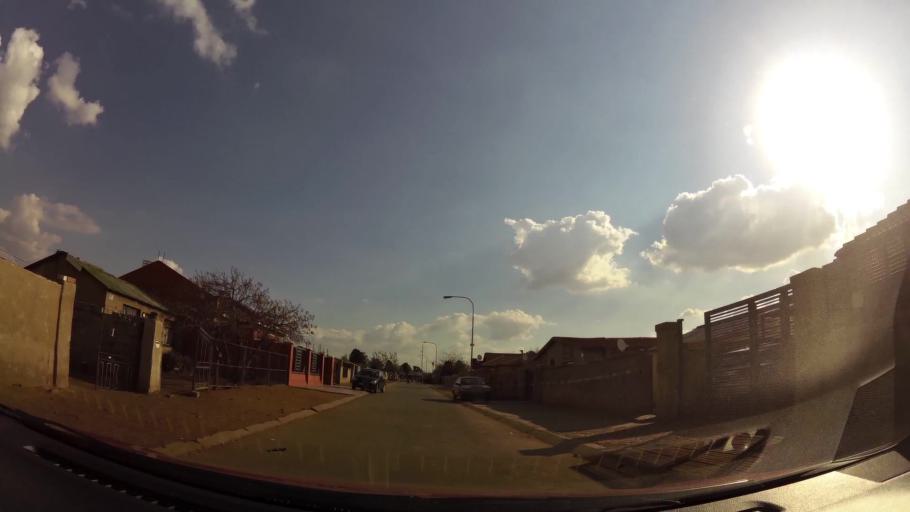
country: ZA
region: Gauteng
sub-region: City of Johannesburg Metropolitan Municipality
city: Soweto
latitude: -26.2243
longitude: 27.8668
